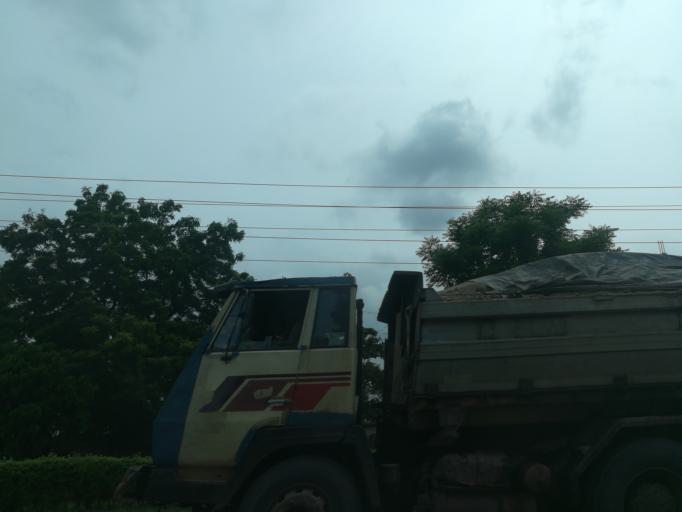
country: NG
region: Lagos
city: Ojota
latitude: 6.6089
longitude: 3.3686
